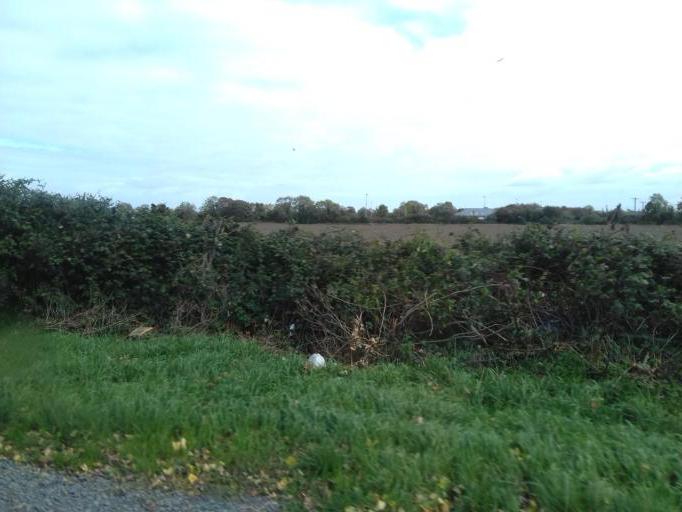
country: IE
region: Leinster
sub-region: Dublin City
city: Finglas
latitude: 53.4107
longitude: -6.2986
